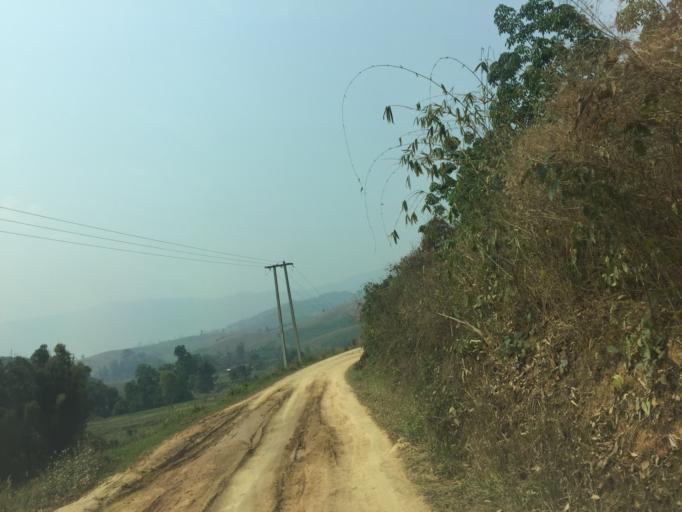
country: TH
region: Phayao
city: Phu Sang
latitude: 19.5960
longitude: 100.5300
